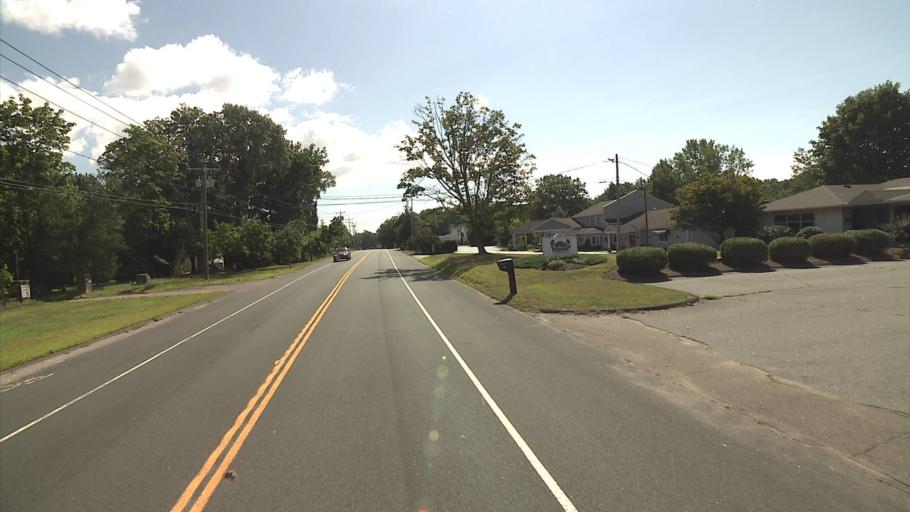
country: US
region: Connecticut
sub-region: New Haven County
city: Guilford
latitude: 41.3082
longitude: -72.7221
